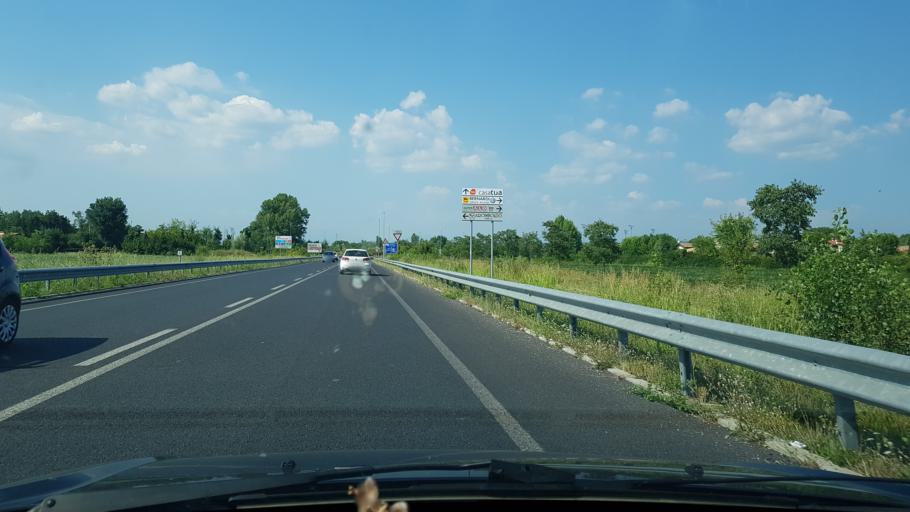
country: IT
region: Friuli Venezia Giulia
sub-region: Provincia di Gorizia
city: Staranzano
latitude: 45.8031
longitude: 13.4882
